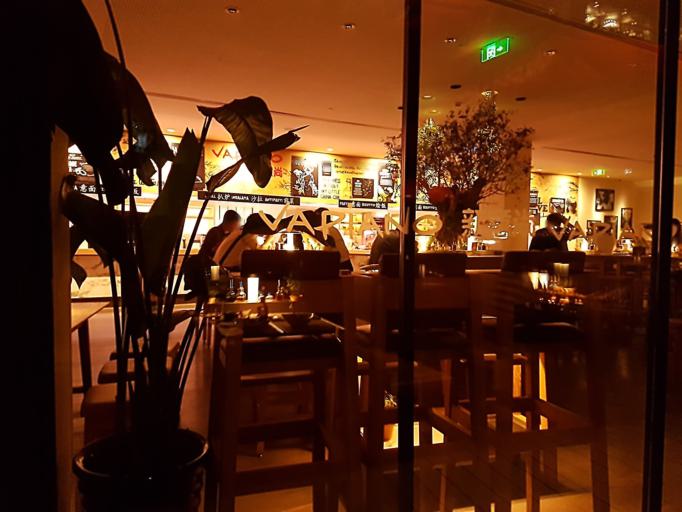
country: CN
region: Shanghai Shi
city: Hongkou
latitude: 31.2376
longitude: 121.4936
